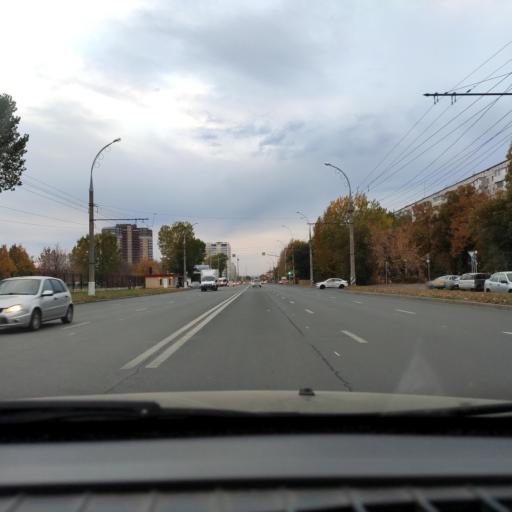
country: RU
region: Samara
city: Tol'yatti
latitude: 53.5080
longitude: 49.2621
